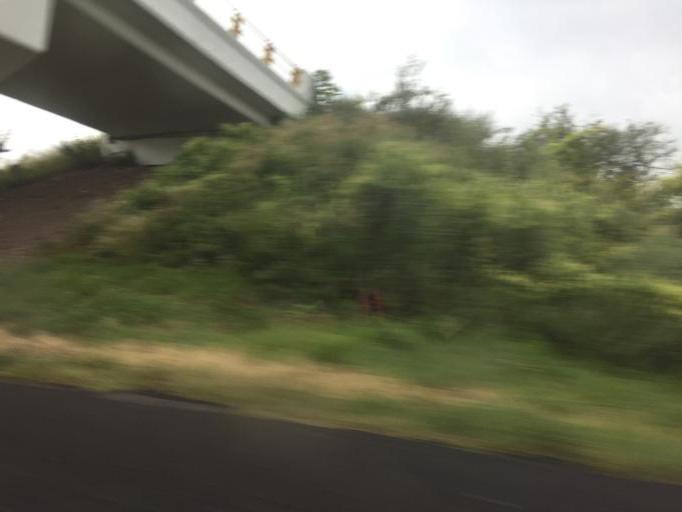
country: MX
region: Jalisco
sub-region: Zapotlan del Rey
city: Zapotlan del Rey
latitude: 20.4549
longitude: -102.8912
